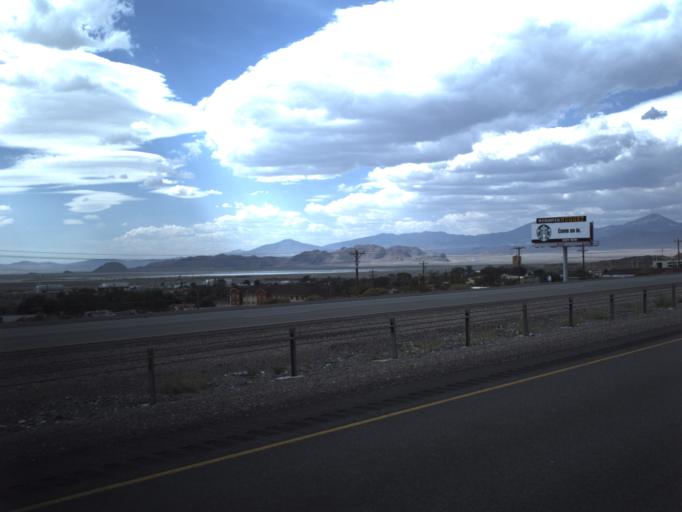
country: US
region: Utah
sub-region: Tooele County
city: Wendover
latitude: 40.7413
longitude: -114.0323
